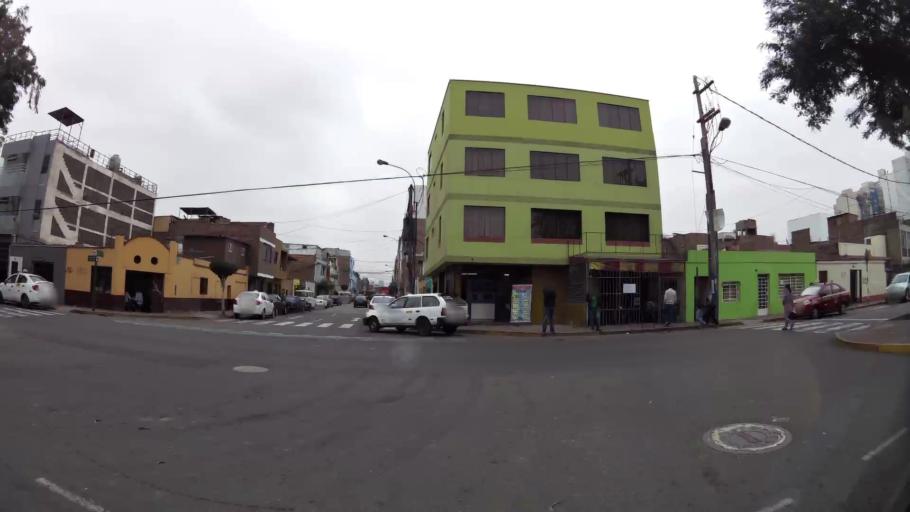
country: PE
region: Lima
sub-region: Lima
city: Surco
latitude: -12.1194
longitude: -77.0192
